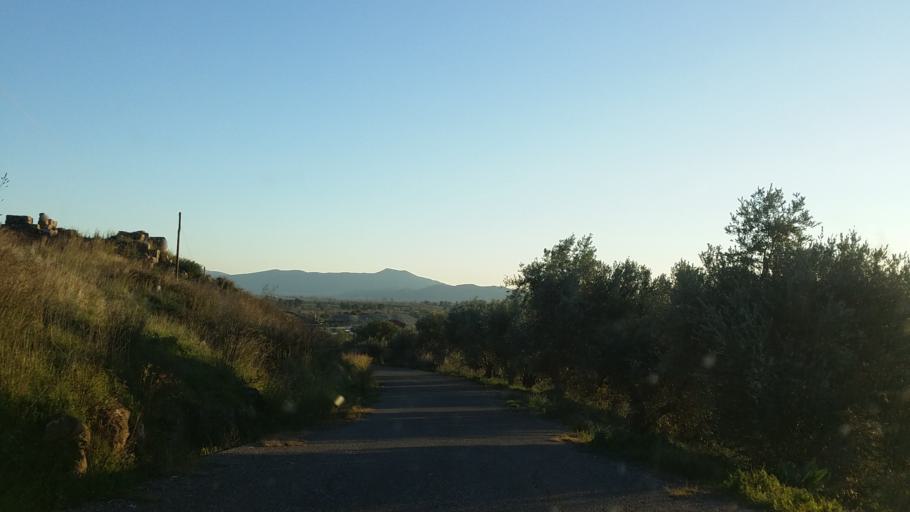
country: GR
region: West Greece
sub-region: Nomos Aitolias kai Akarnanias
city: Neapolis
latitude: 38.6701
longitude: 21.3178
